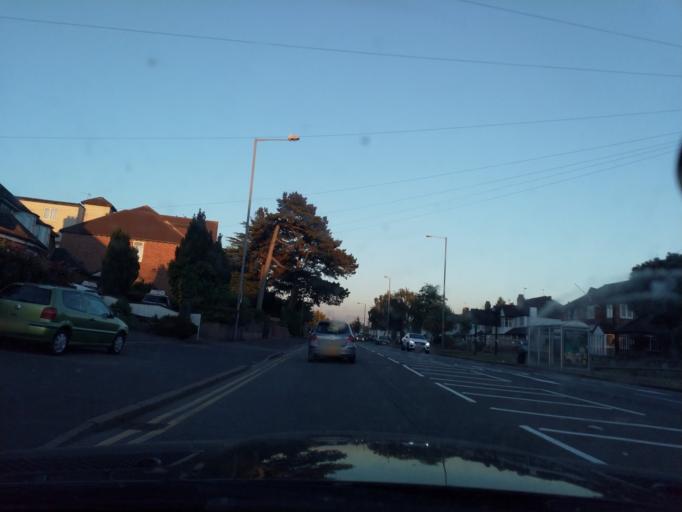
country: GB
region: England
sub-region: City and Borough of Birmingham
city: Acocks Green
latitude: 52.4507
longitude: -1.8305
